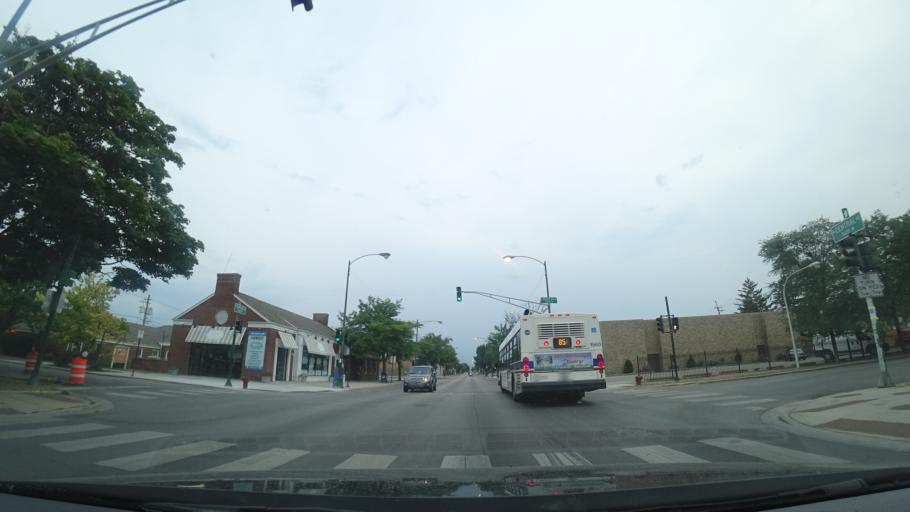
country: US
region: Illinois
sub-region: Cook County
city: Harwood Heights
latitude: 41.9566
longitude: -87.7671
